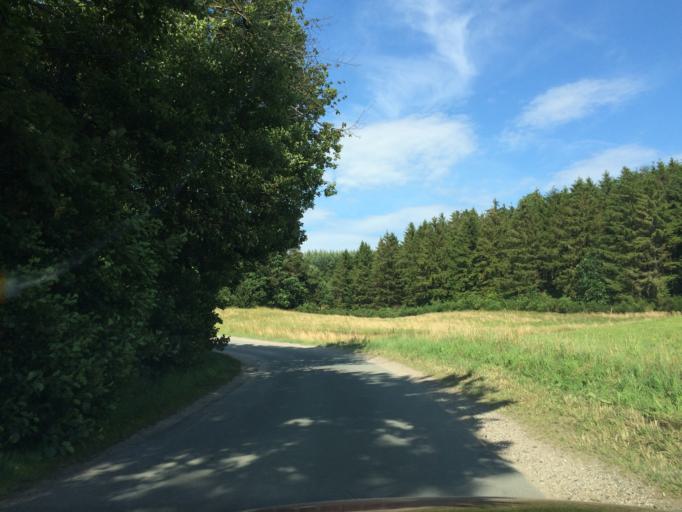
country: DK
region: Central Jutland
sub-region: Syddjurs Kommune
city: Ebeltoft
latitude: 56.2659
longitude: 10.7437
